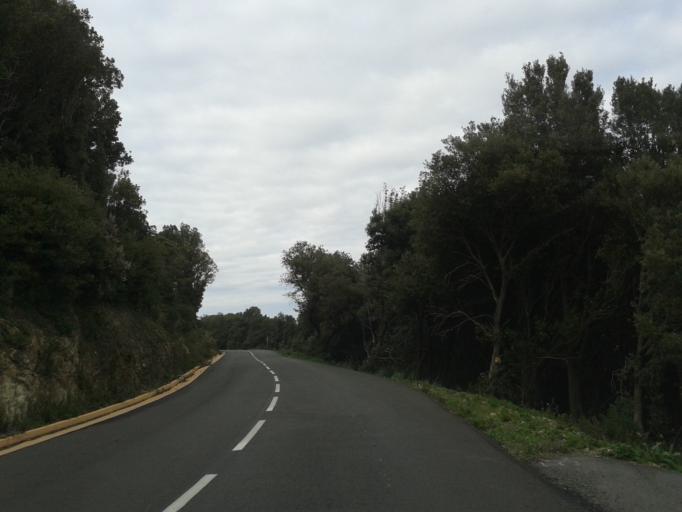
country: FR
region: Corsica
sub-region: Departement de la Haute-Corse
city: Brando
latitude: 42.9714
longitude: 9.3864
